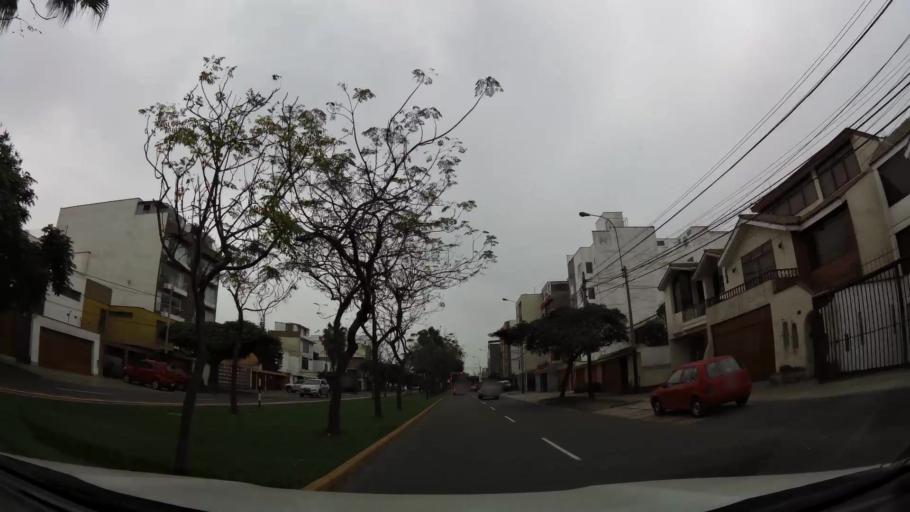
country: PE
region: Lima
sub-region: Lima
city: Surco
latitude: -12.1322
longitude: -76.9892
